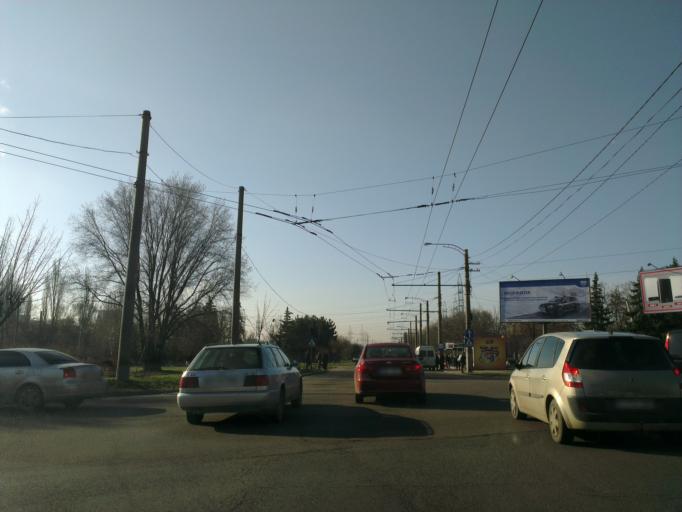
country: MD
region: Chisinau
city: Chisinau
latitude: 47.0332
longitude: 28.8888
